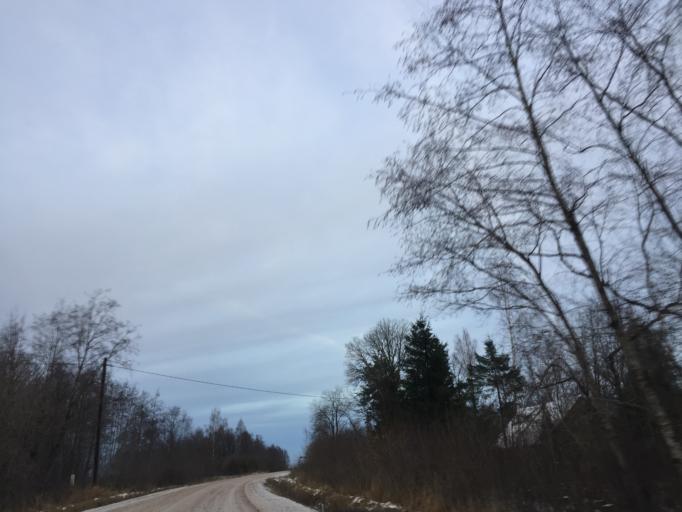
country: LV
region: Limbazu Rajons
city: Limbazi
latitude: 57.5771
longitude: 24.8277
